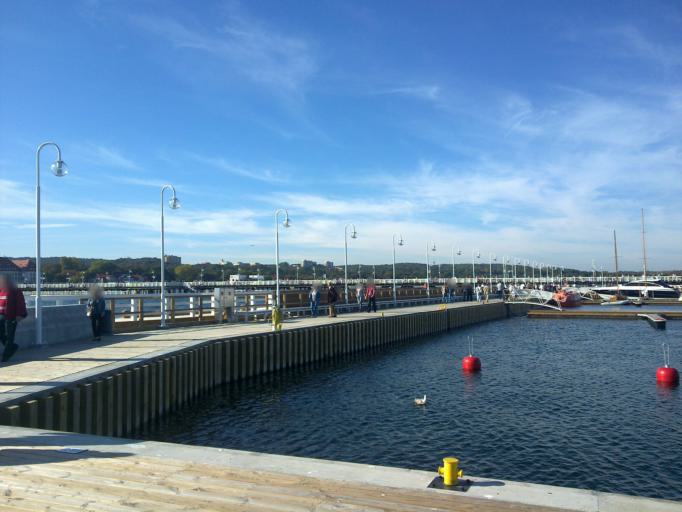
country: PL
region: Pomeranian Voivodeship
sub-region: Sopot
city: Sopot
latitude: 54.4468
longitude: 18.5776
